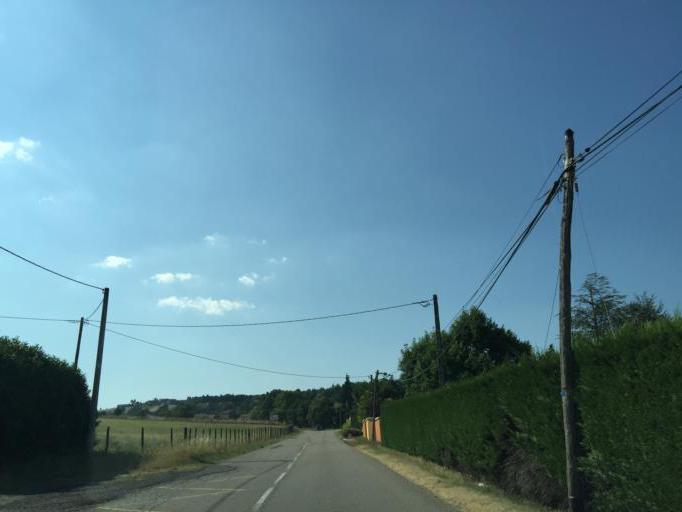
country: FR
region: Rhone-Alpes
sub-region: Departement de la Loire
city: Saint-Chamond
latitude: 45.4889
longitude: 4.4914
